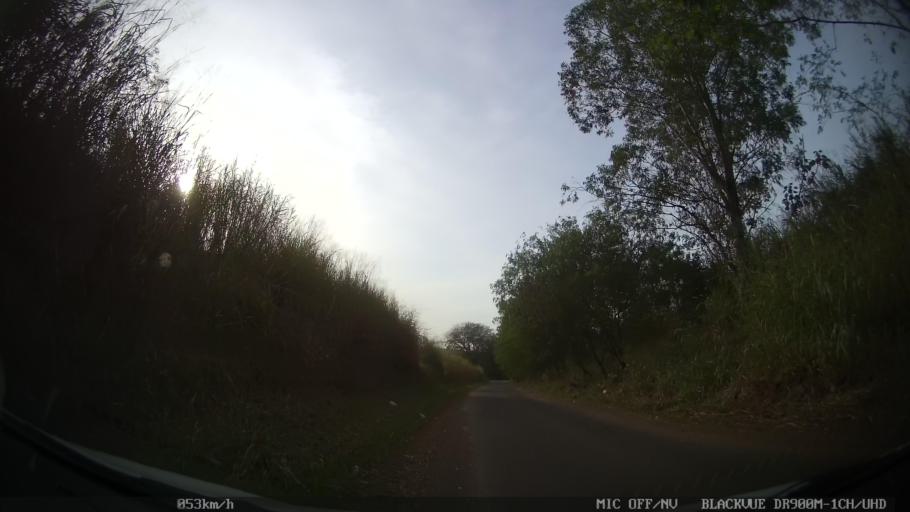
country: BR
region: Sao Paulo
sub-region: Piracicaba
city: Piracicaba
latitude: -22.7017
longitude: -47.5879
